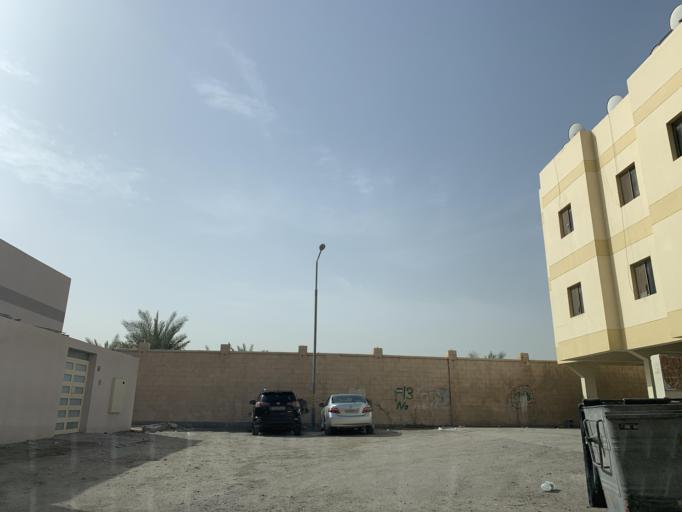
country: BH
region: Northern
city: Madinat `Isa
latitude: 26.1782
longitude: 50.5664
